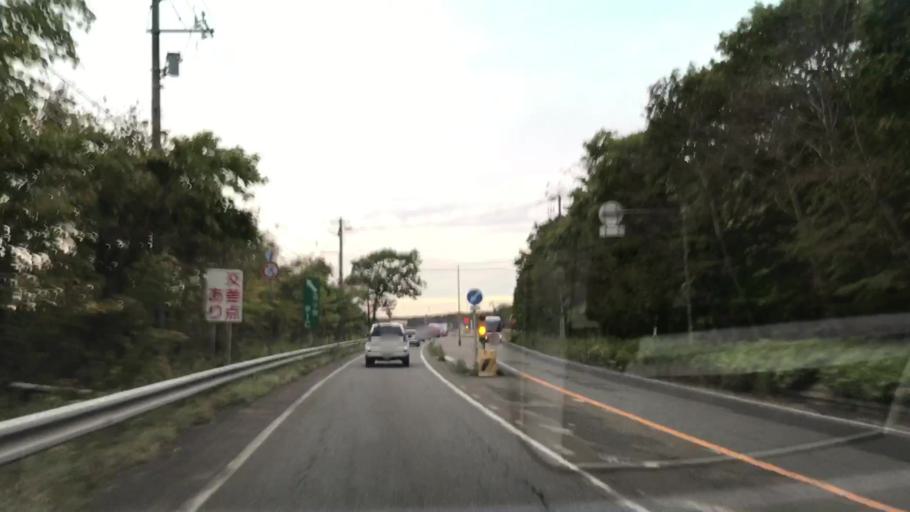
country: JP
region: Hokkaido
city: Tomakomai
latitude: 42.7066
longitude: 141.6620
